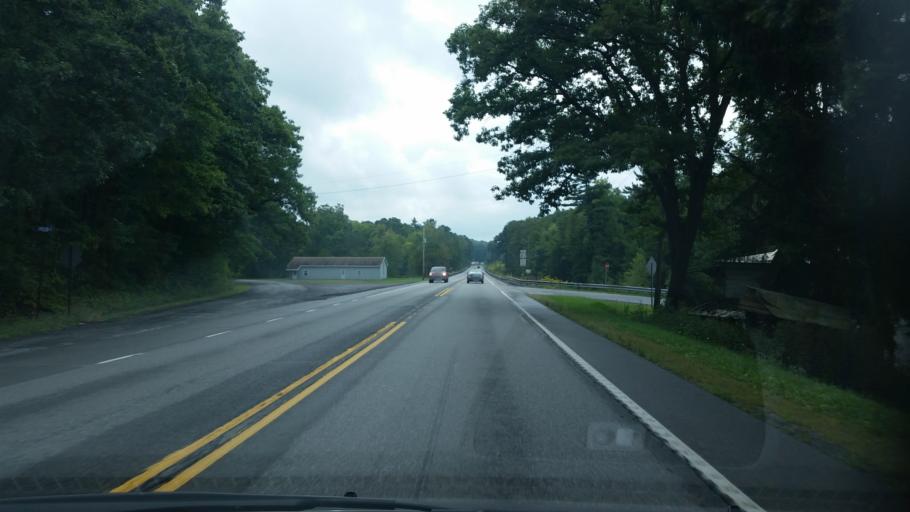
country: US
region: Pennsylvania
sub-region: Clearfield County
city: Troy
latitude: 40.9481
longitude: -78.2909
